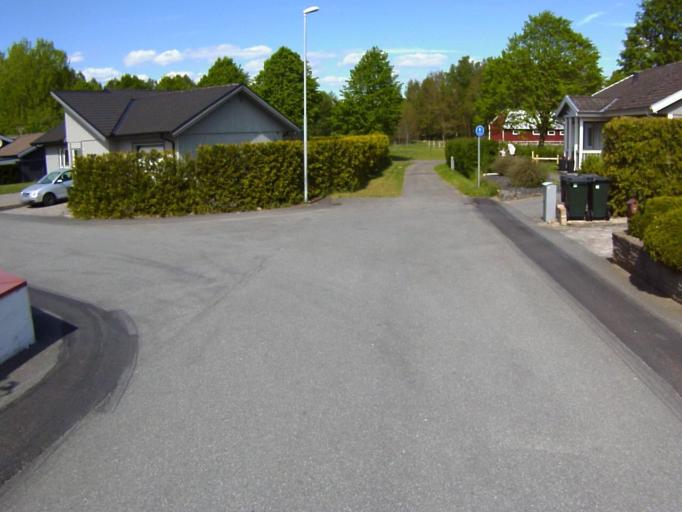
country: SE
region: Skane
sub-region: Ostra Goinge Kommun
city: Hanaskog
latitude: 56.0791
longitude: 14.0928
